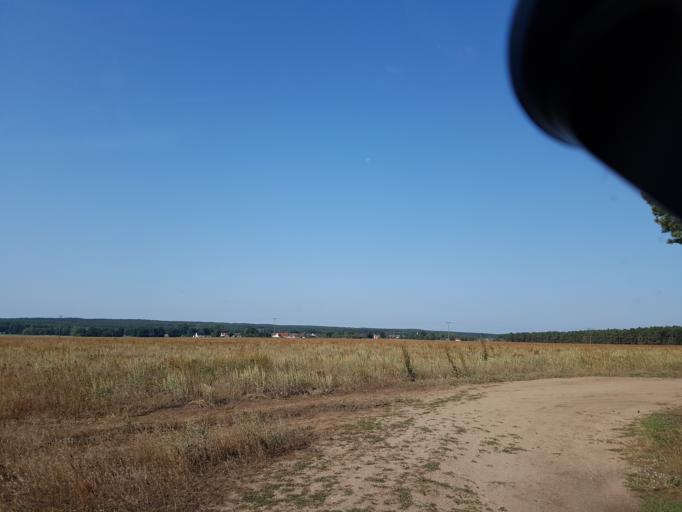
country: DE
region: Brandenburg
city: Wollin
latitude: 52.2503
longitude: 12.5035
